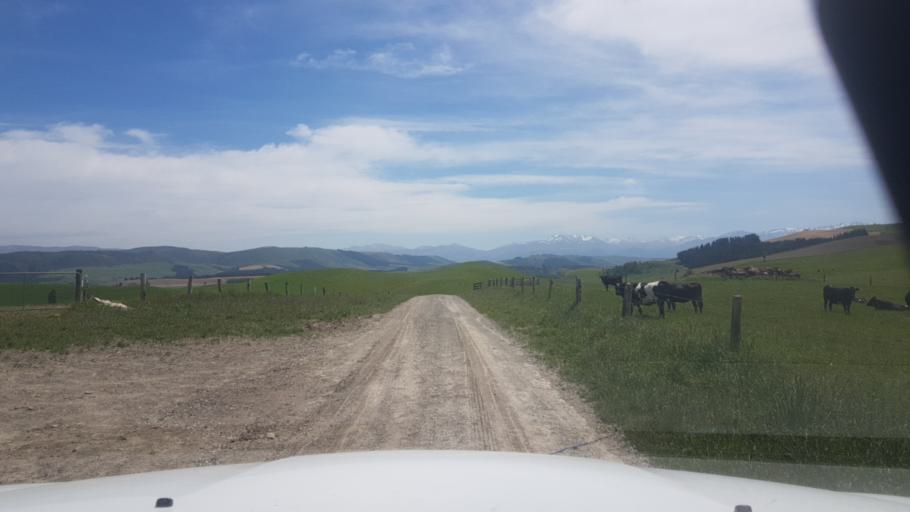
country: NZ
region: Canterbury
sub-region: Timaru District
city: Pleasant Point
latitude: -44.1295
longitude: 171.0143
